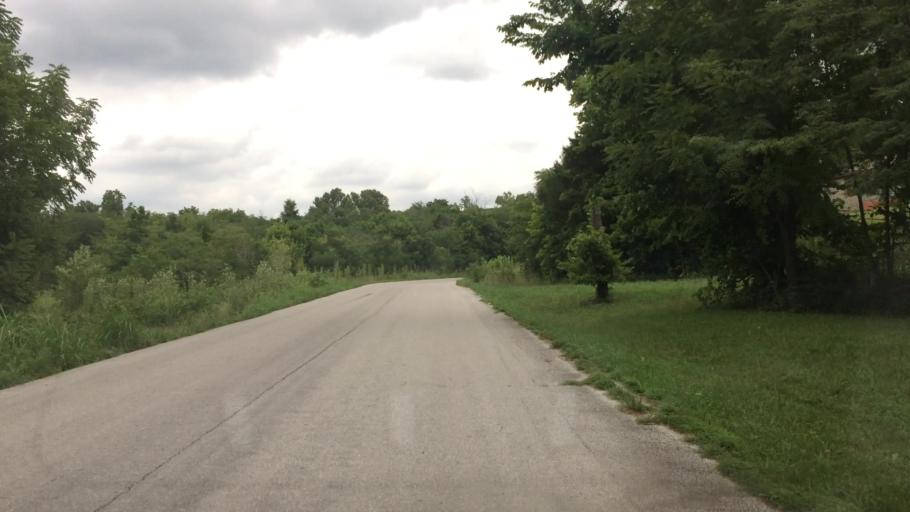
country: US
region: Missouri
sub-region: Greene County
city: Strafford
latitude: 37.3260
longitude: -93.0566
